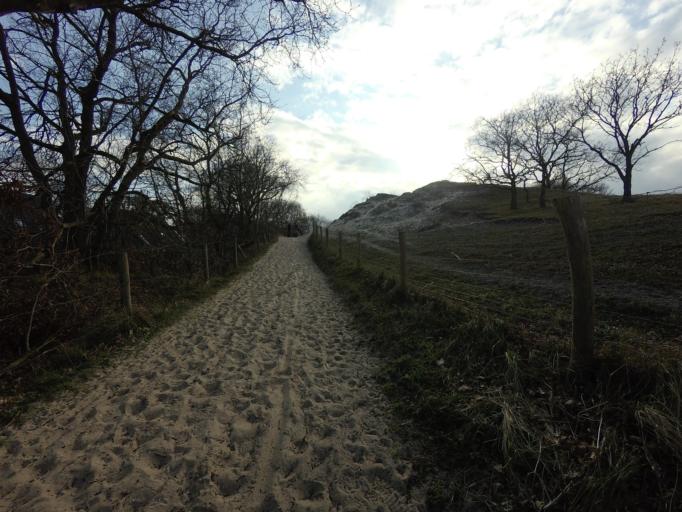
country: NL
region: Zeeland
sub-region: Schouwen-Duiveland
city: Burgh
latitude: 51.6868
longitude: 3.7216
